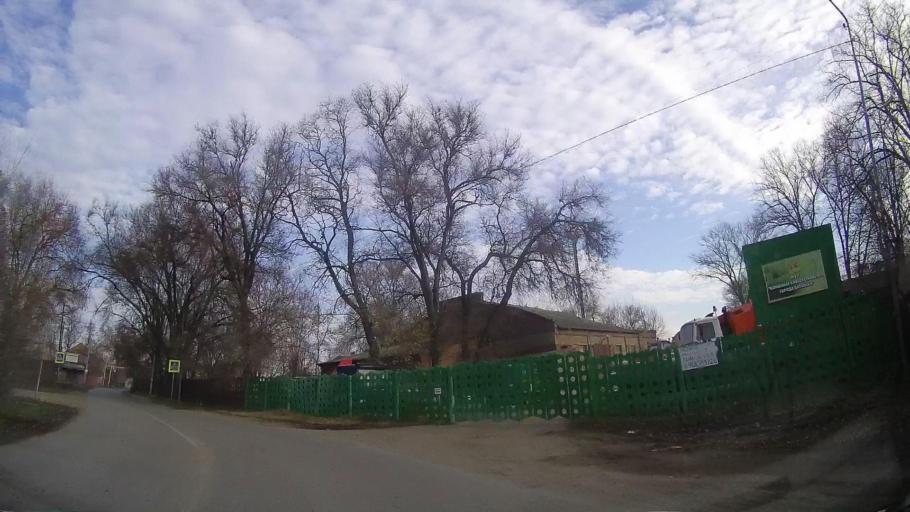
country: RU
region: Rostov
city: Bataysk
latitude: 47.1286
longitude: 39.7839
